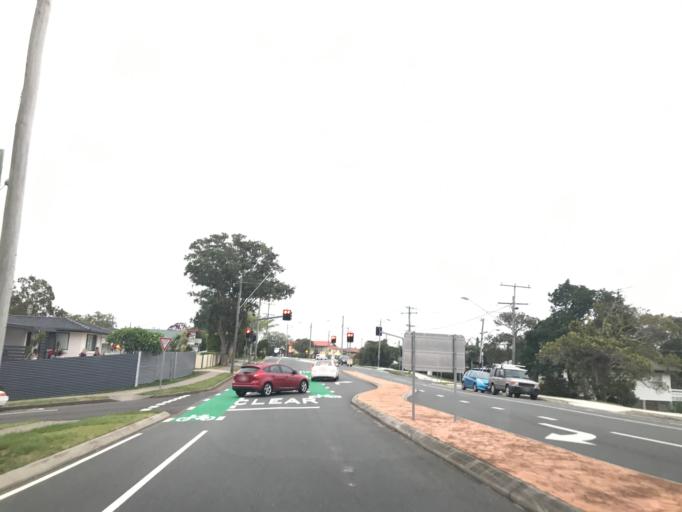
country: AU
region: Queensland
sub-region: Sunshine Coast
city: Dicky Beach
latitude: -26.7980
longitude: 153.1376
